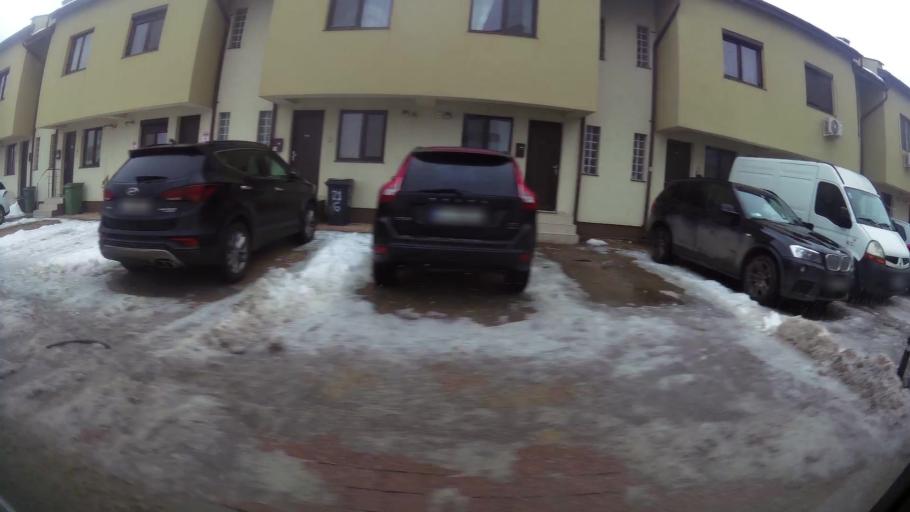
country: RO
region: Ilfov
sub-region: Comuna Chiajna
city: Chiajna
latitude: 44.4519
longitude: 25.9836
